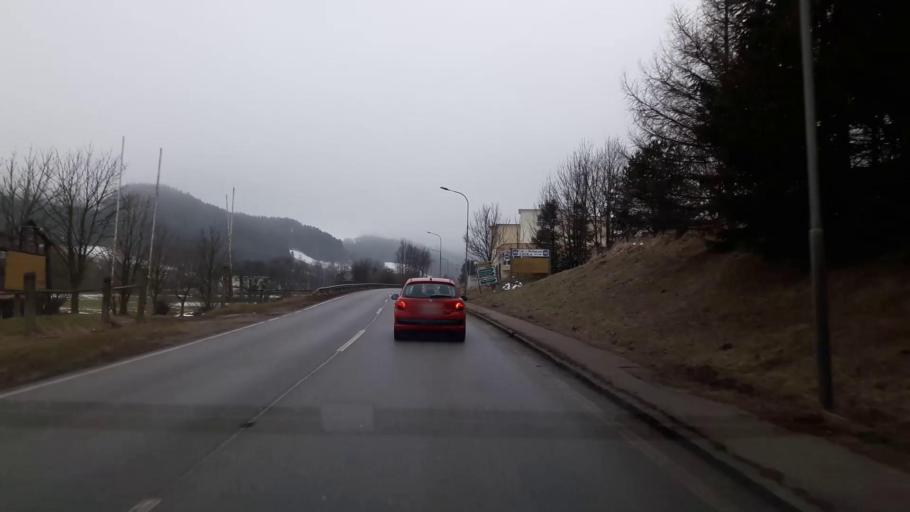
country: AT
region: Lower Austria
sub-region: Politischer Bezirk Neunkirchen
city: Edlitz
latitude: 47.5774
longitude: 16.0994
